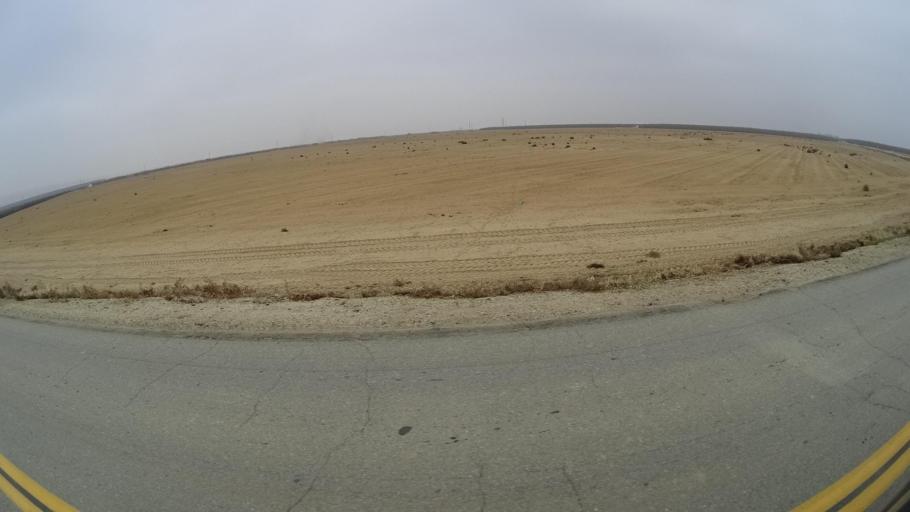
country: US
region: California
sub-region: Kern County
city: Maricopa
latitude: 35.1021
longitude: -119.3400
